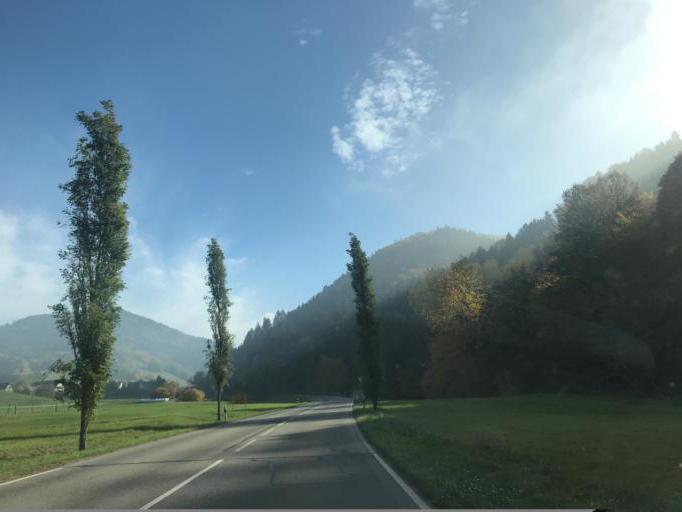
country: DE
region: Baden-Wuerttemberg
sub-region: Freiburg Region
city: Glottertal
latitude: 48.0465
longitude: 7.9695
